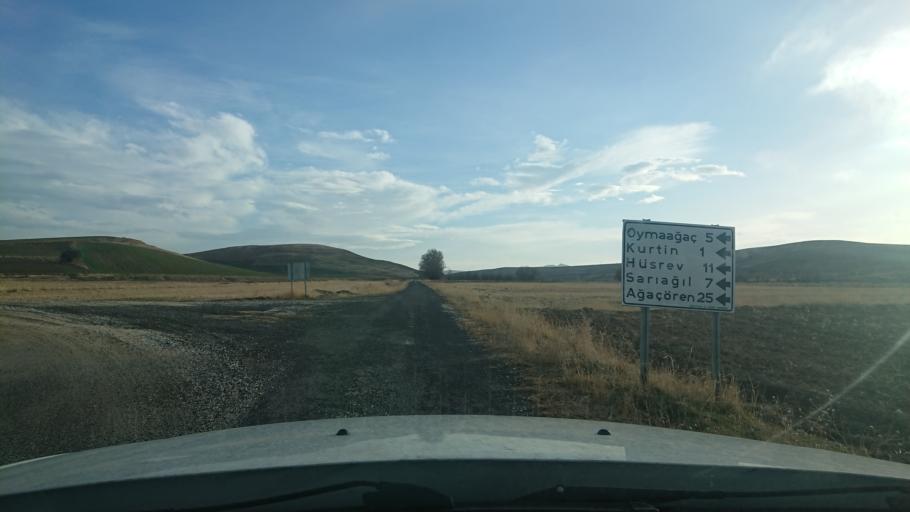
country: TR
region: Aksaray
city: Acipinar
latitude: 38.6844
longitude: 33.8696
